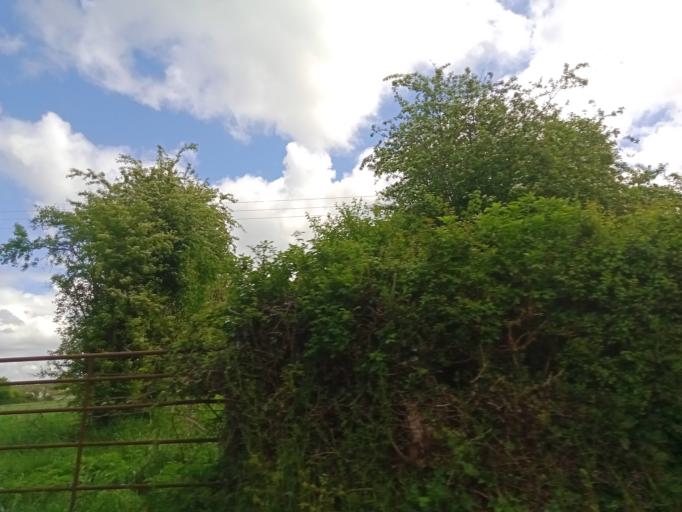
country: IE
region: Munster
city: Thurles
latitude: 52.6722
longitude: -7.6761
